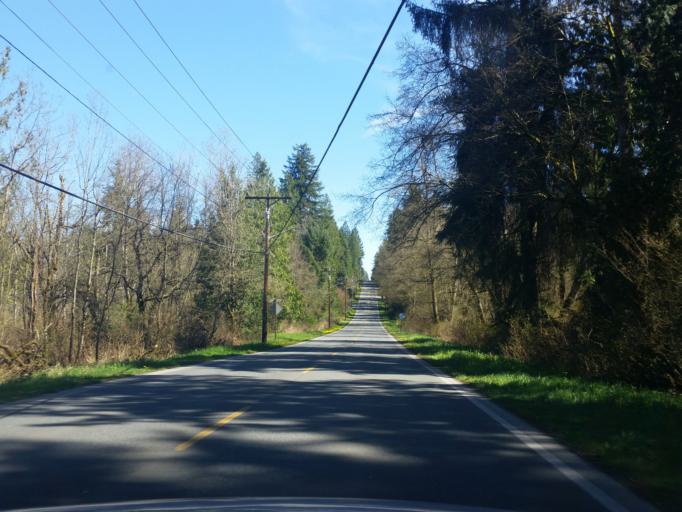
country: US
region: Washington
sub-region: Snohomish County
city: North Creek
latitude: 47.8343
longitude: -122.1629
